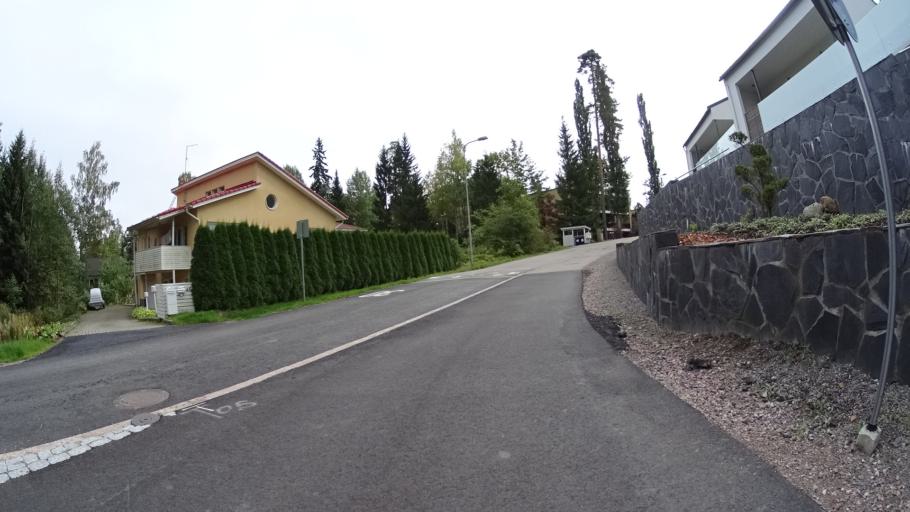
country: FI
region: Uusimaa
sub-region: Helsinki
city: Kauniainen
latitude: 60.2201
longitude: 24.7364
